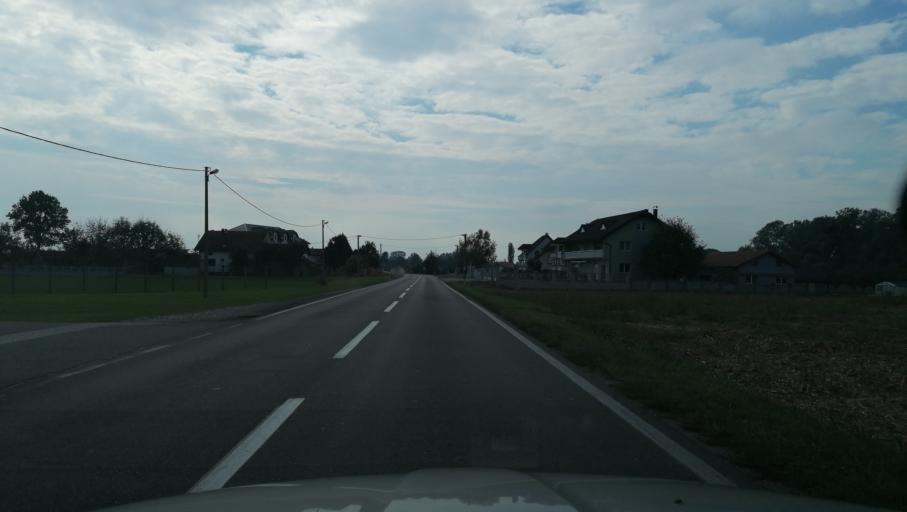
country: BA
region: Republika Srpska
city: Dvorovi
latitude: 44.8249
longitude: 19.2829
